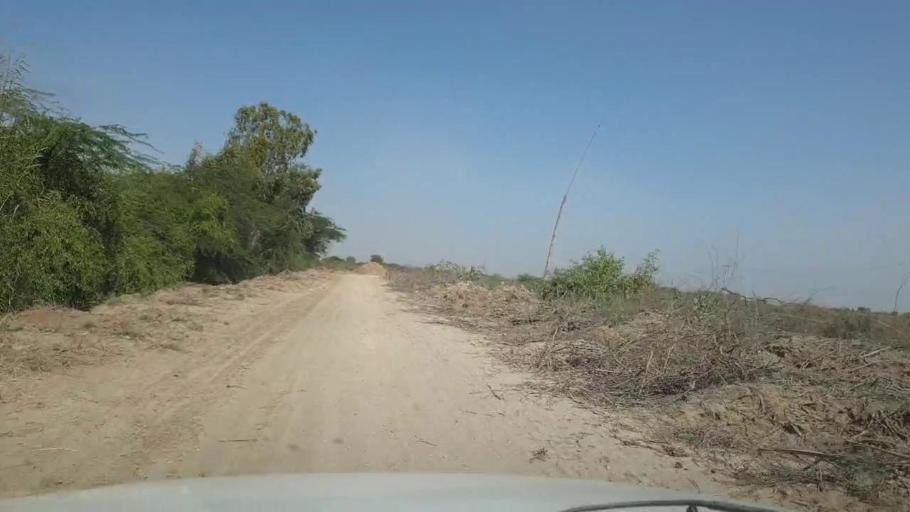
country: PK
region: Sindh
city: Mirpur Sakro
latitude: 24.3989
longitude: 67.7574
